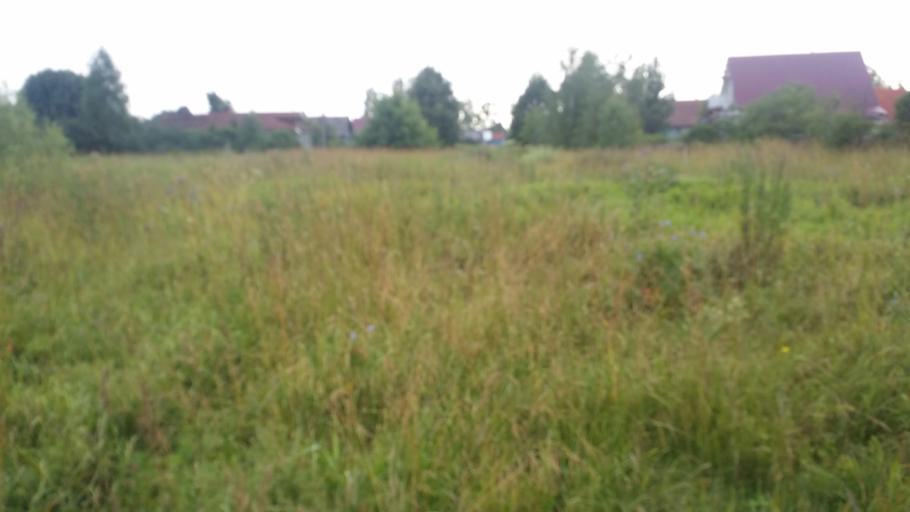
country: RU
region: Vladimir
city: Stavrovo
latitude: 56.3227
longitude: 39.8865
